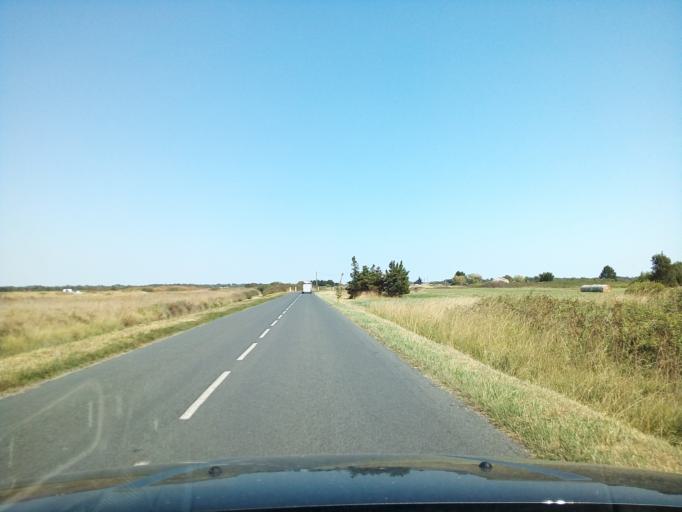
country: FR
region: Poitou-Charentes
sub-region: Departement de la Charente-Maritime
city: Boyard-Ville
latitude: 45.9691
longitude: -1.2792
